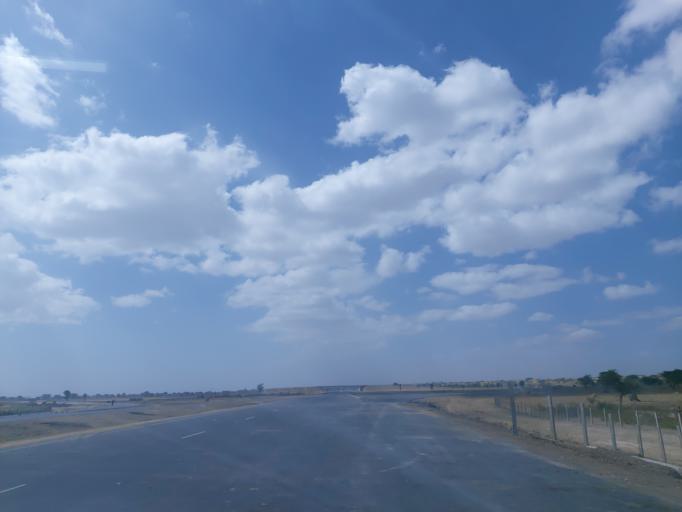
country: ET
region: Oromiya
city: Ziway
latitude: 8.1531
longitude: 38.8016
